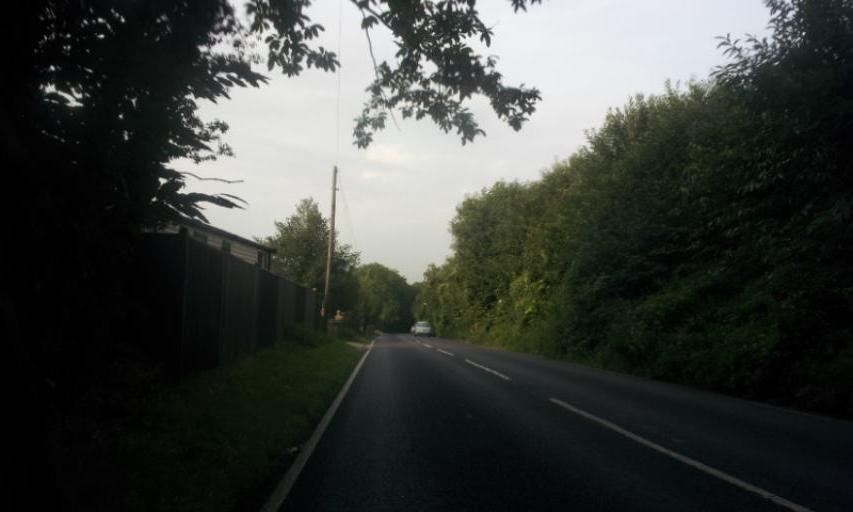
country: GB
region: England
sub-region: Kent
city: Larkfield
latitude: 51.2753
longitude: 0.4340
